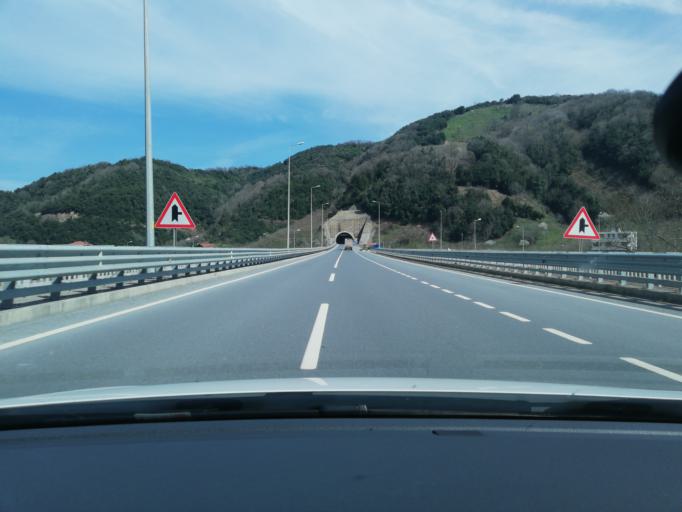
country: TR
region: Zonguldak
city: Alapli
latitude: 41.1515
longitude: 31.3518
